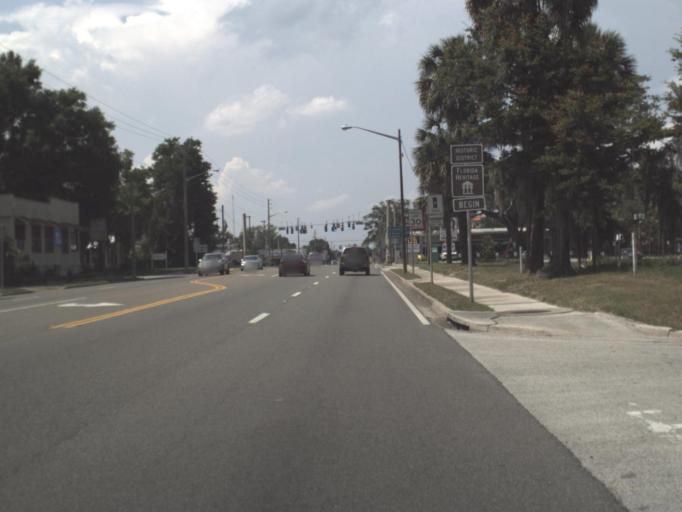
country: US
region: Florida
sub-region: Clay County
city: Green Cove Springs
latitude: 29.9905
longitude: -81.6784
